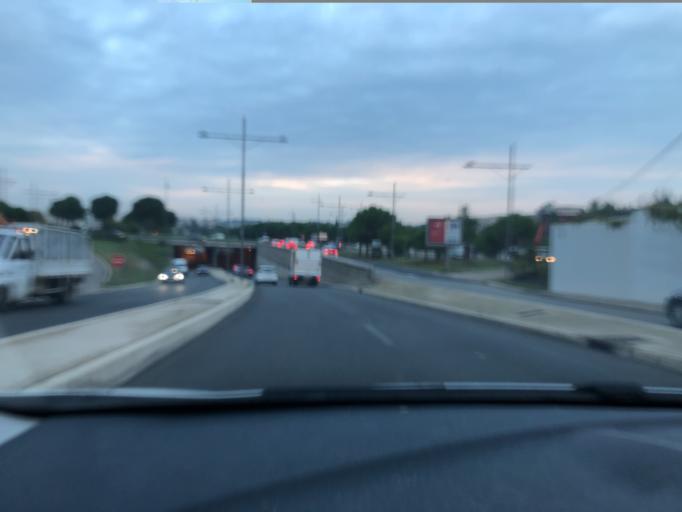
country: FR
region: Languedoc-Roussillon
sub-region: Departement de l'Herault
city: Montferrier-sur-Lez
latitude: 43.6425
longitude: 3.8478
